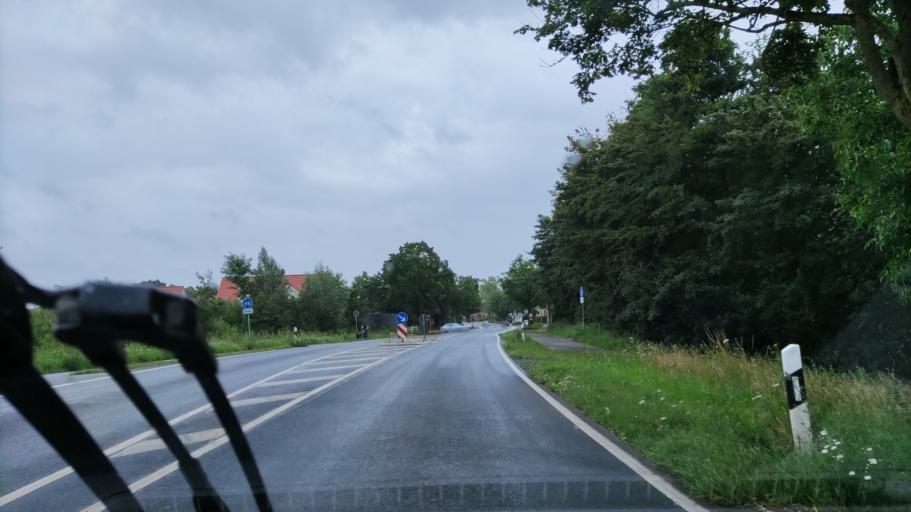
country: DE
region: North Rhine-Westphalia
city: Ahlen
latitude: 51.7713
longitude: 7.8706
